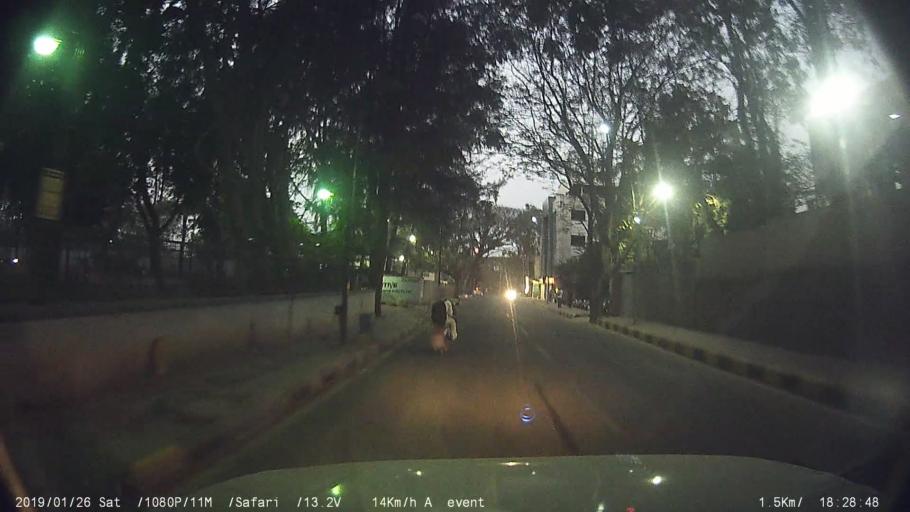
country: IN
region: Karnataka
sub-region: Bangalore Urban
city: Anekal
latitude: 12.8471
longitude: 77.6621
